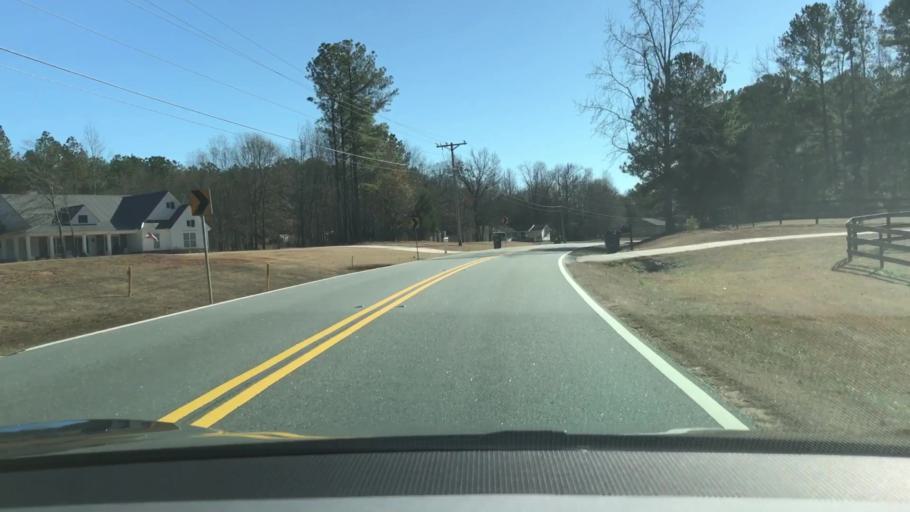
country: US
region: Georgia
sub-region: Walton County
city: Monroe
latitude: 33.8576
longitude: -83.7379
